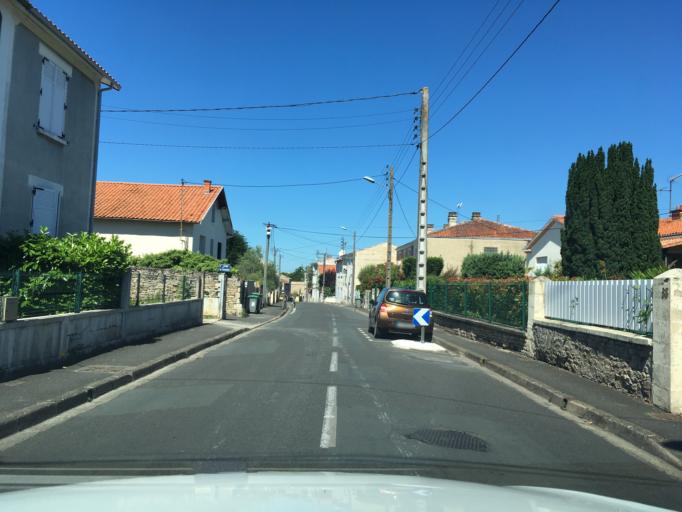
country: FR
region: Poitou-Charentes
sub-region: Departement des Deux-Sevres
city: Niort
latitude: 46.3265
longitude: -0.4400
